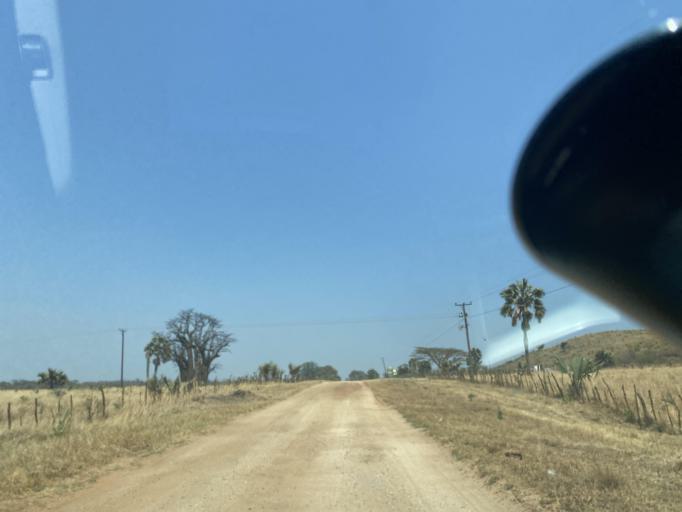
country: ZM
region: Lusaka
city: Lusaka
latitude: -15.5363
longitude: 28.0866
